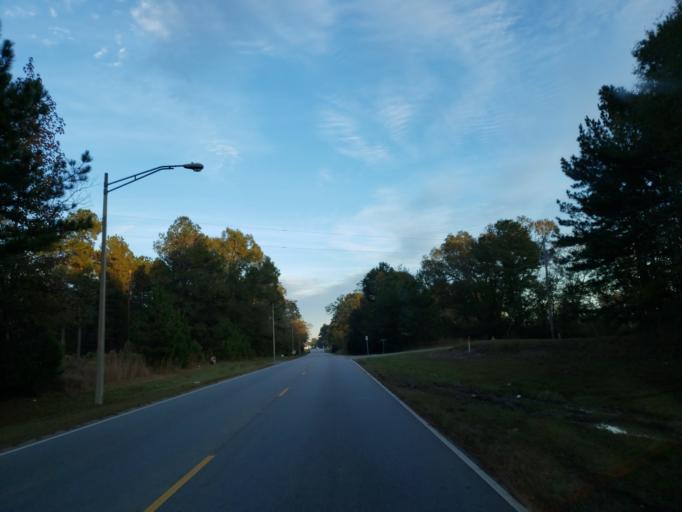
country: US
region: Mississippi
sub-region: Forrest County
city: Hattiesburg
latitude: 31.2665
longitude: -89.2785
